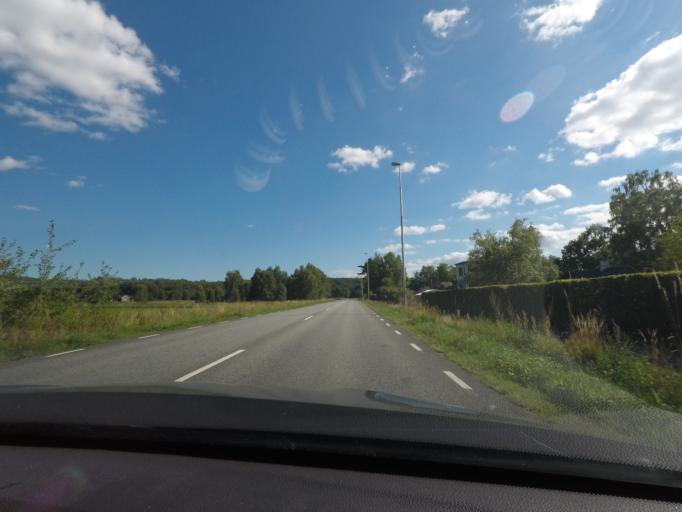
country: SE
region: Skane
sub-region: Hassleholms Kommun
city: Tormestorp
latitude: 56.1320
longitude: 13.7398
